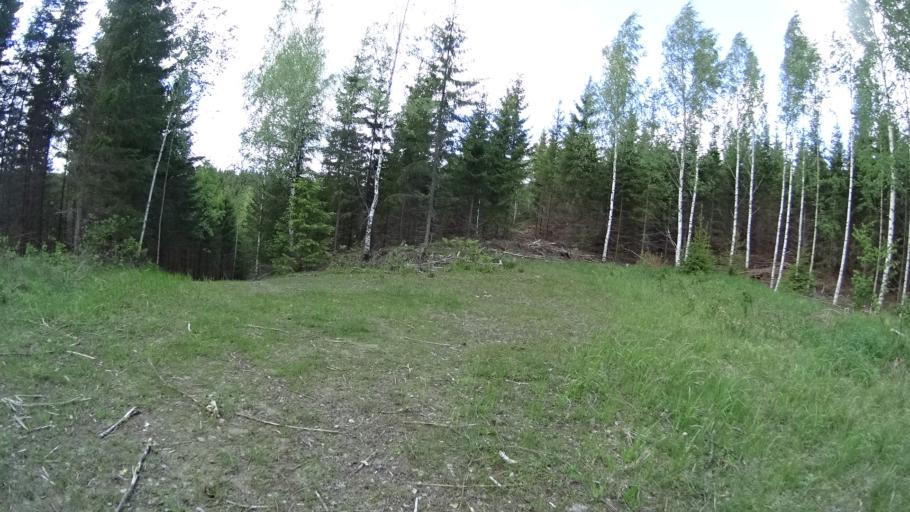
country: FI
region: Uusimaa
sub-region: Raaseporin
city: Pohja
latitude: 60.1630
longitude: 23.6076
